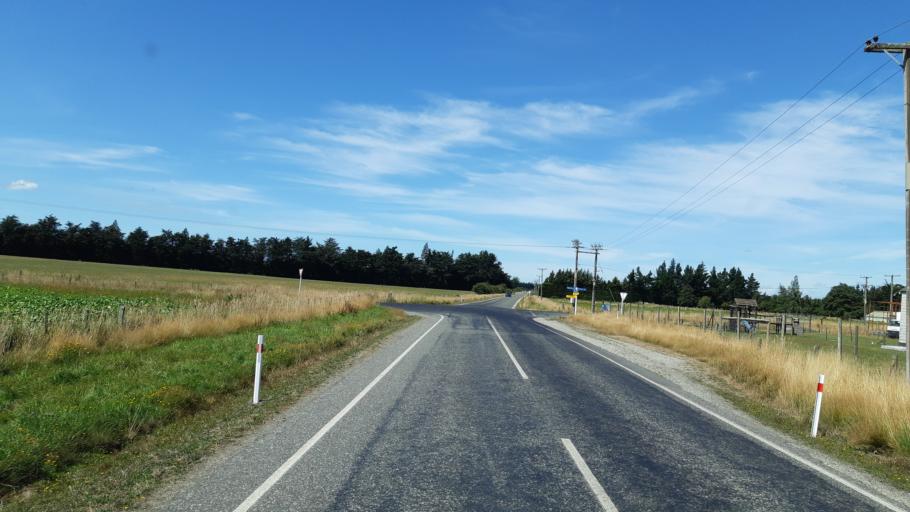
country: NZ
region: Southland
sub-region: Gore District
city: Gore
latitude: -46.0075
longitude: 168.9163
